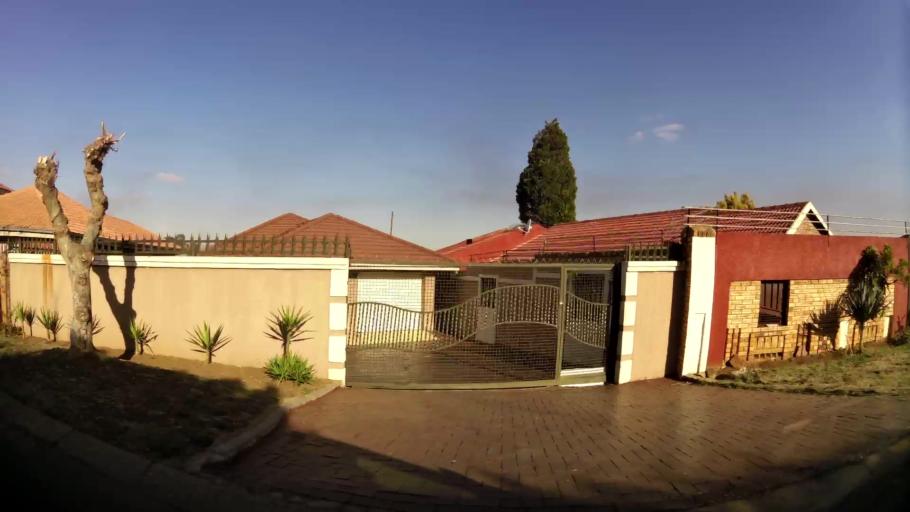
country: ZA
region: Gauteng
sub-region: City of Johannesburg Metropolitan Municipality
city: Soweto
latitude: -26.2746
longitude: 27.9147
